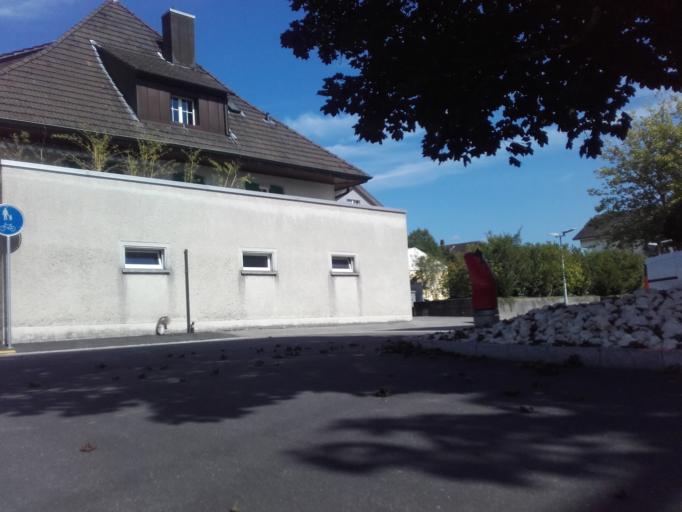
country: CH
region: Solothurn
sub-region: Bezirk Lebern
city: Riedholz
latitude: 47.2197
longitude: 7.5542
